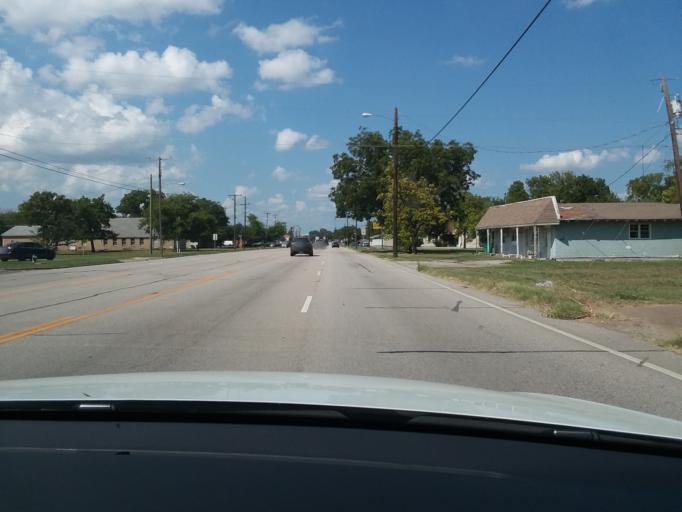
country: US
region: Texas
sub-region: Collin County
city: McKinney
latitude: 33.2009
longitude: -96.6120
